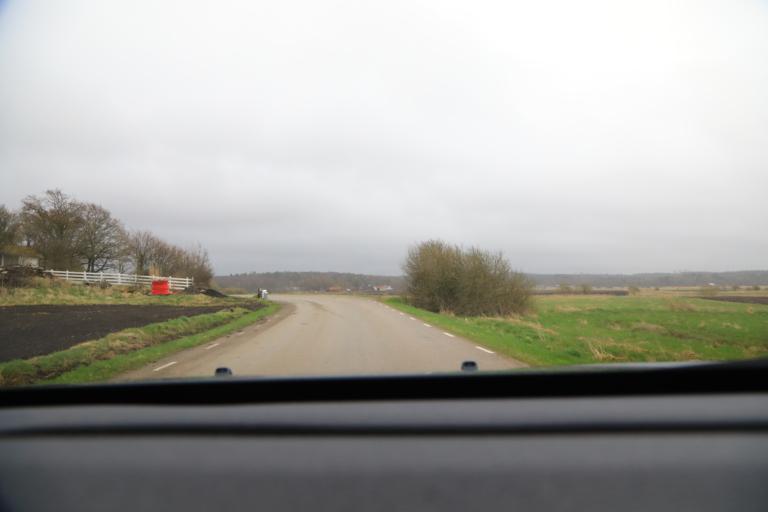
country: SE
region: Halland
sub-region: Kungsbacka Kommun
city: Frillesas
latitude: 57.2983
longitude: 12.1909
